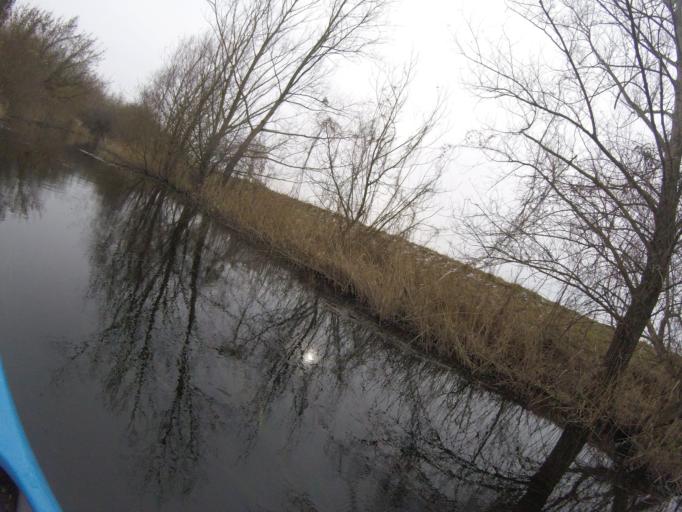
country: HU
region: Zala
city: Keszthely
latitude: 46.7530
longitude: 17.2157
